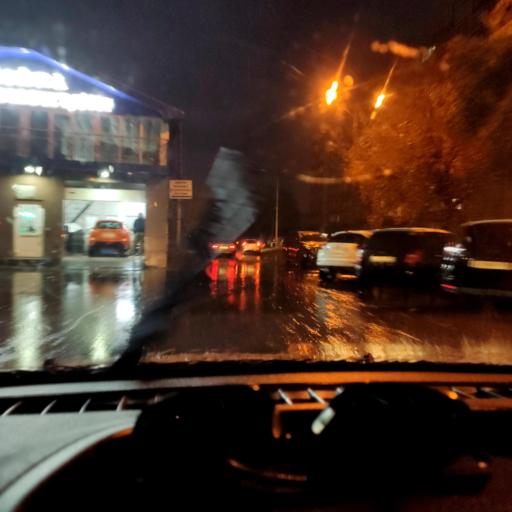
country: RU
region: Samara
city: Zhigulevsk
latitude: 53.4814
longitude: 49.4873
